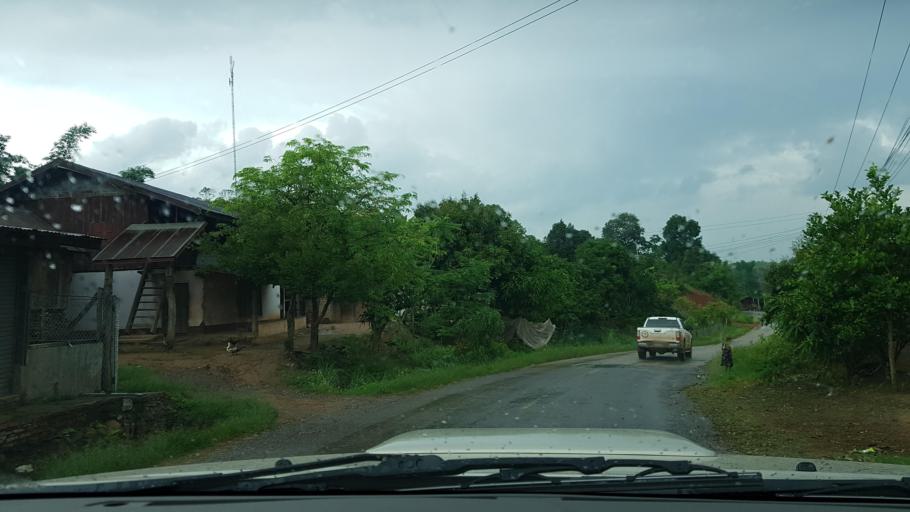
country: LA
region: Oudomxai
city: Muang Xay
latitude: 20.5725
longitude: 101.9204
